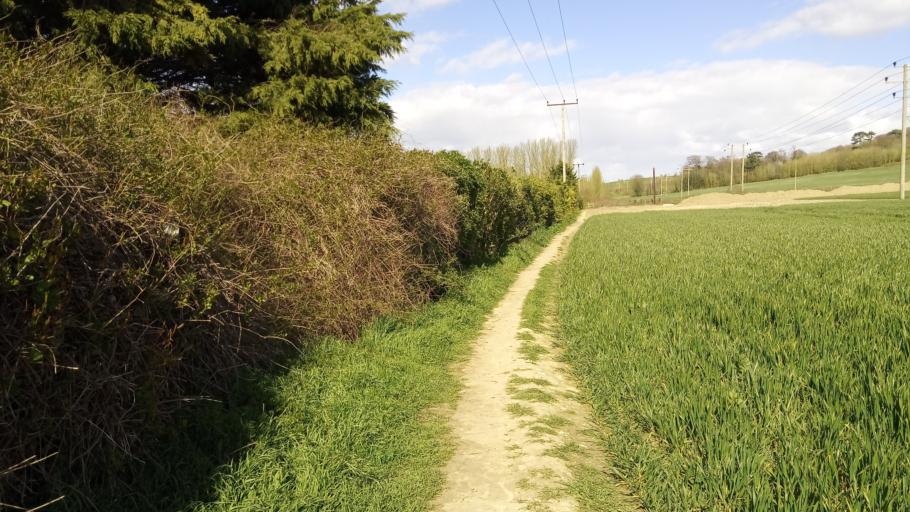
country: GB
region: England
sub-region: Kent
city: Chartham
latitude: 51.2580
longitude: 1.0332
